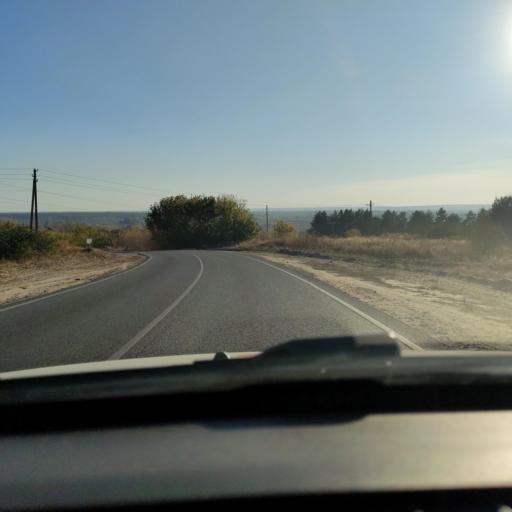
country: RU
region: Voronezj
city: Shilovo
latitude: 51.5549
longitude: 39.1327
